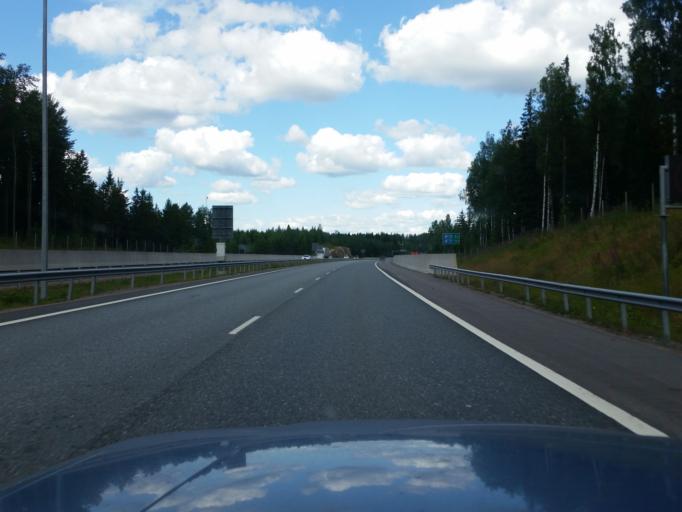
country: FI
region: Uusimaa
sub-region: Helsinki
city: Sammatti
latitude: 60.3470
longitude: 23.9028
